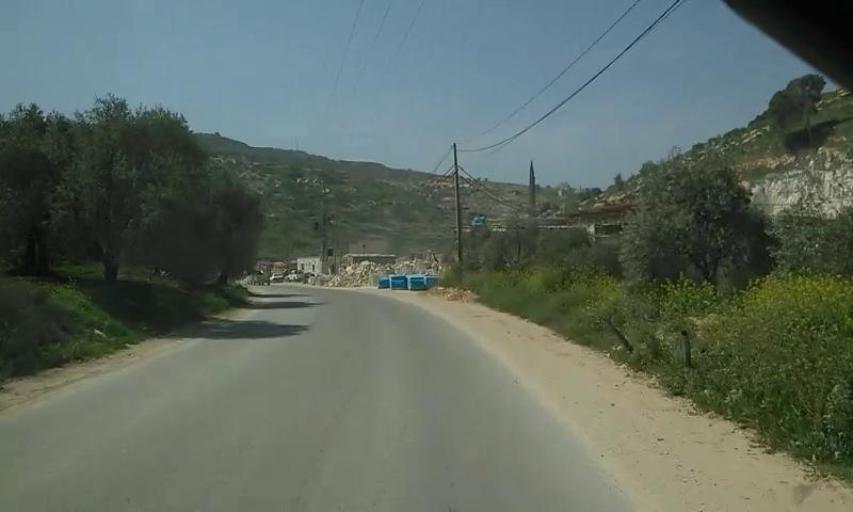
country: PS
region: West Bank
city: Qabatiyah
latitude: 32.4054
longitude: 35.2939
